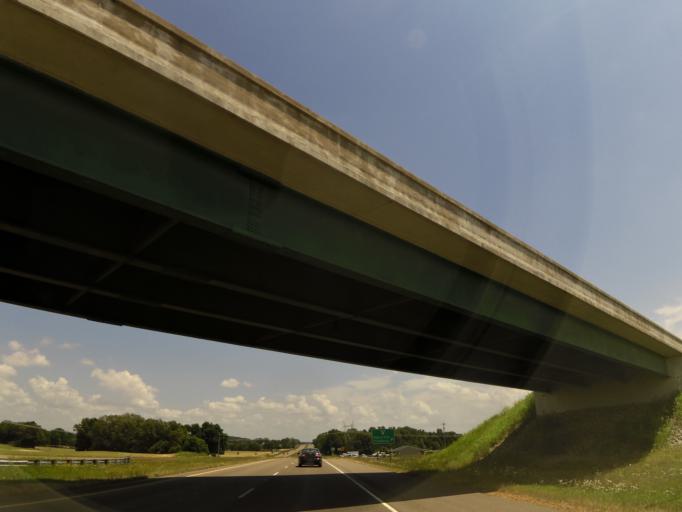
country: US
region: Tennessee
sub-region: Crockett County
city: Alamo
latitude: 35.8832
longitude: -89.2282
